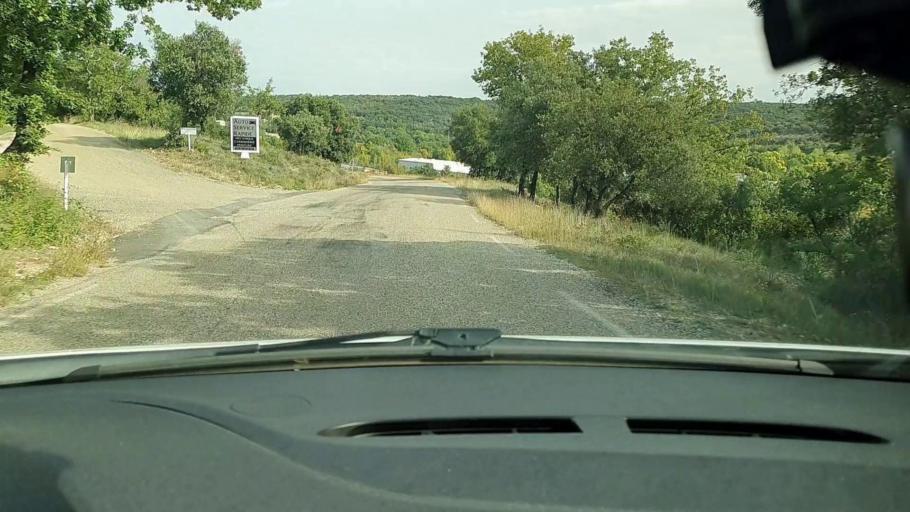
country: FR
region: Languedoc-Roussillon
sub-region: Departement du Gard
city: Saint-Quentin-la-Poterie
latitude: 44.1307
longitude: 4.4017
